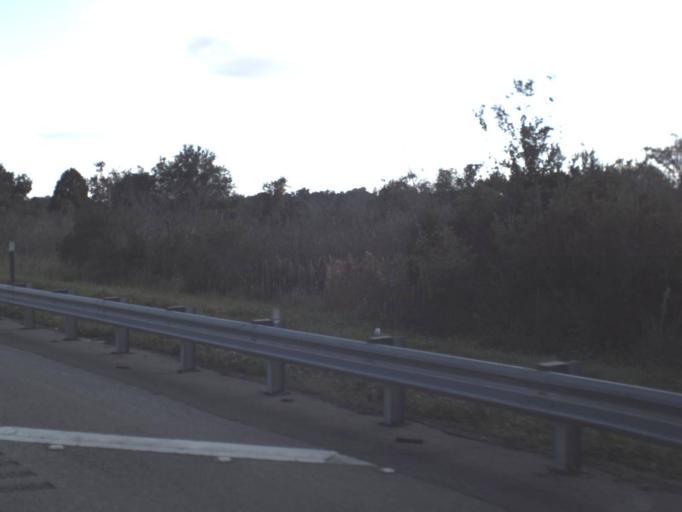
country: US
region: Florida
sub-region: Osceola County
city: Saint Cloud
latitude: 28.0886
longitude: -81.2687
